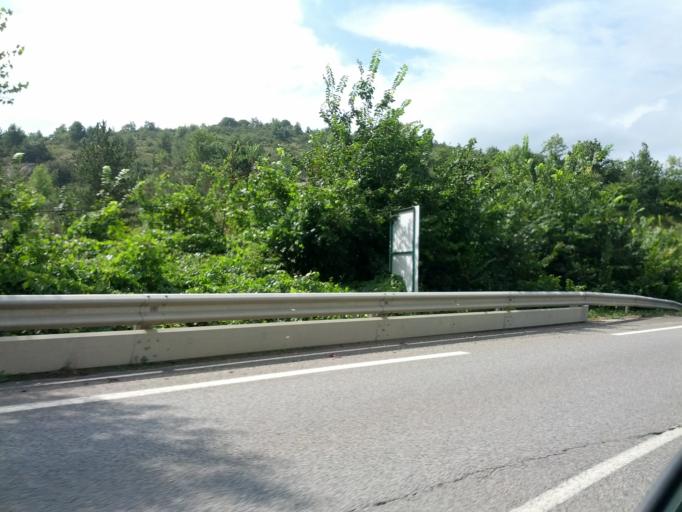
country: FR
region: Languedoc-Roussillon
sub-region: Departement de l'Aude
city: Esperaza
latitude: 42.9338
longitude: 2.2339
